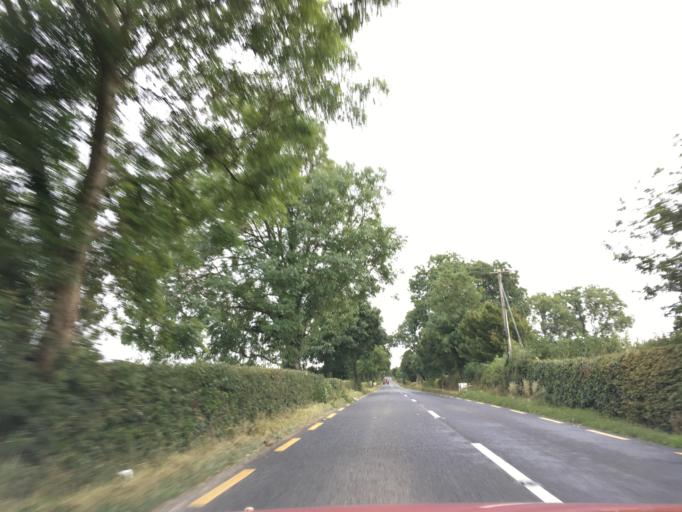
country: IE
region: Munster
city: Fethard
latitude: 52.4363
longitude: -7.7911
